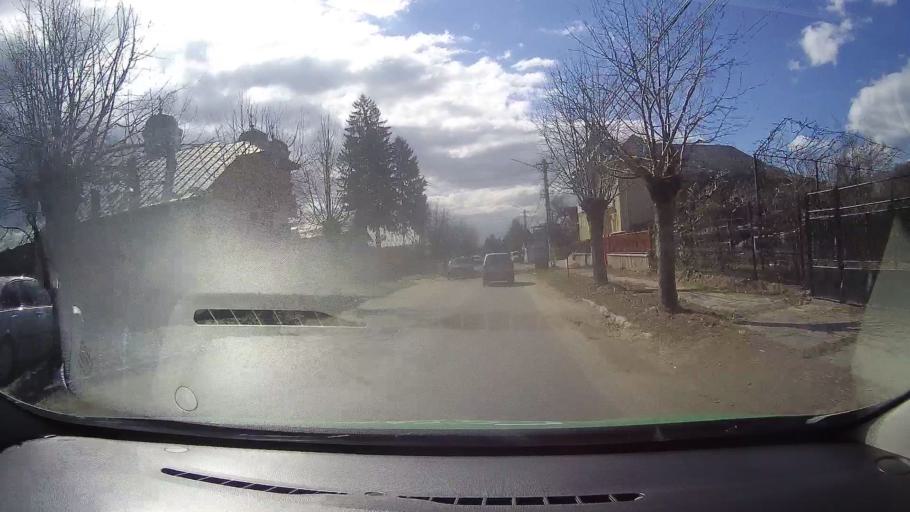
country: RO
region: Dambovita
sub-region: Comuna Branesti
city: Branesti
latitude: 45.0441
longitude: 25.4224
